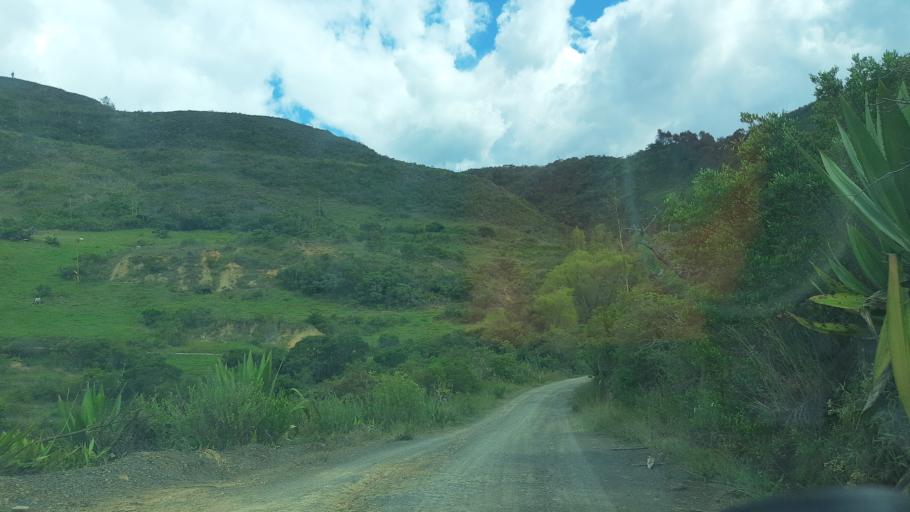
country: CO
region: Boyaca
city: Santa Sofia
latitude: 5.7060
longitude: -73.5610
